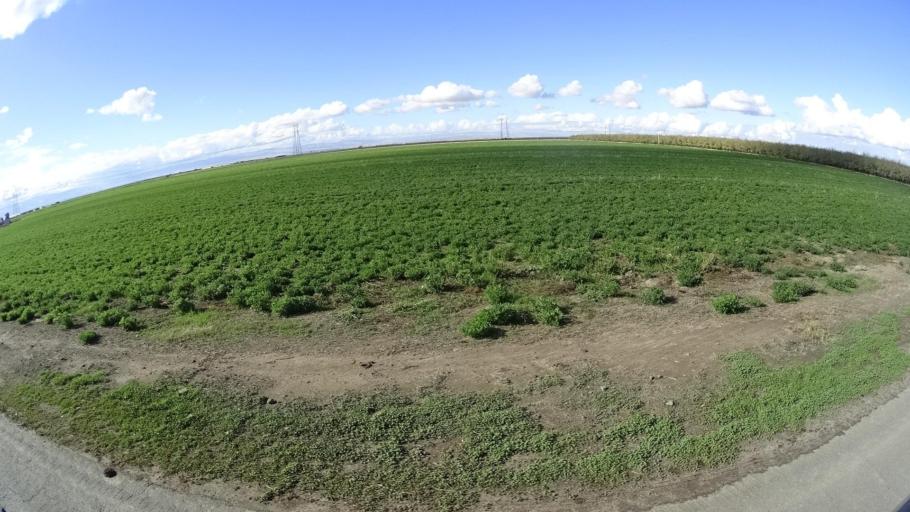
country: US
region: California
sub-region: Kern County
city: Greenacres
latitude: 35.2627
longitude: -119.1284
